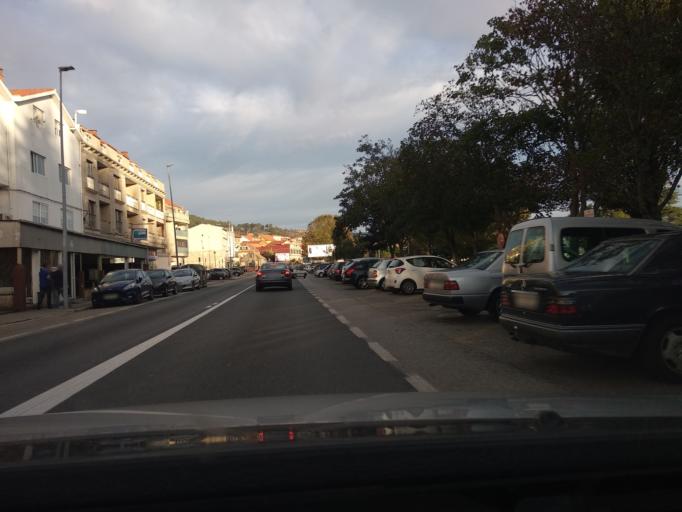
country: ES
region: Galicia
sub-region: Provincia de Pontevedra
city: Moana
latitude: 42.2873
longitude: -8.7265
